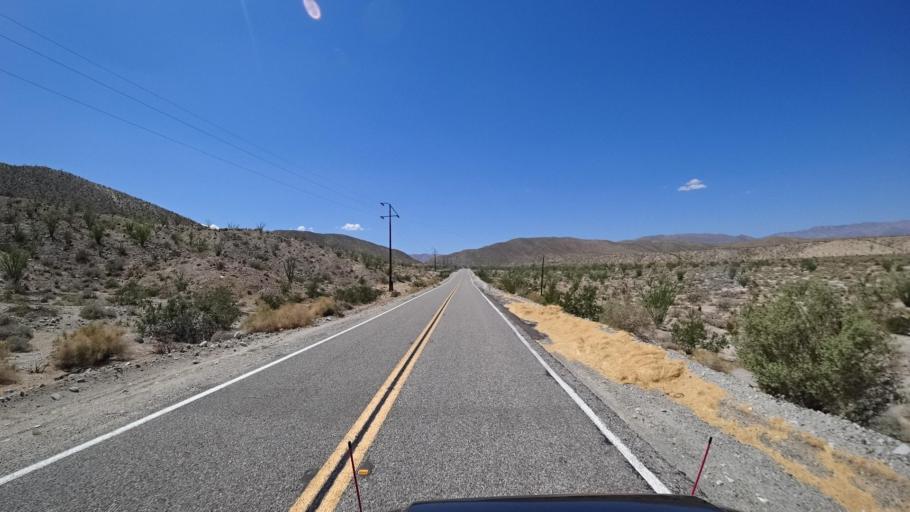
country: US
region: California
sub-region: San Diego County
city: Borrego Springs
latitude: 33.1414
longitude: -116.2825
